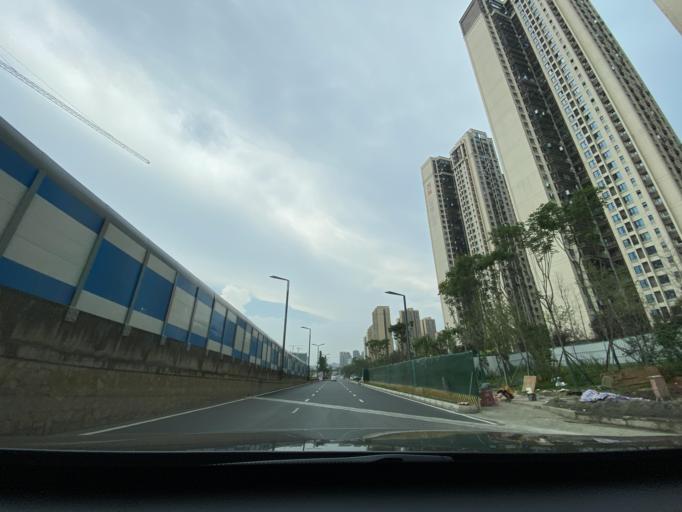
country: CN
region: Sichuan
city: Dongsheng
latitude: 30.4758
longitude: 104.0263
